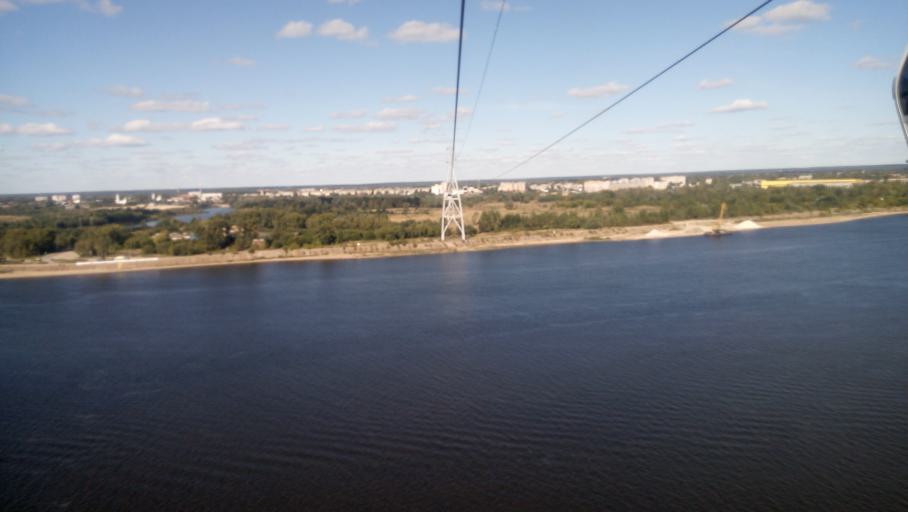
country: RU
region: Nizjnij Novgorod
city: Bor
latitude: 56.3356
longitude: 44.0477
